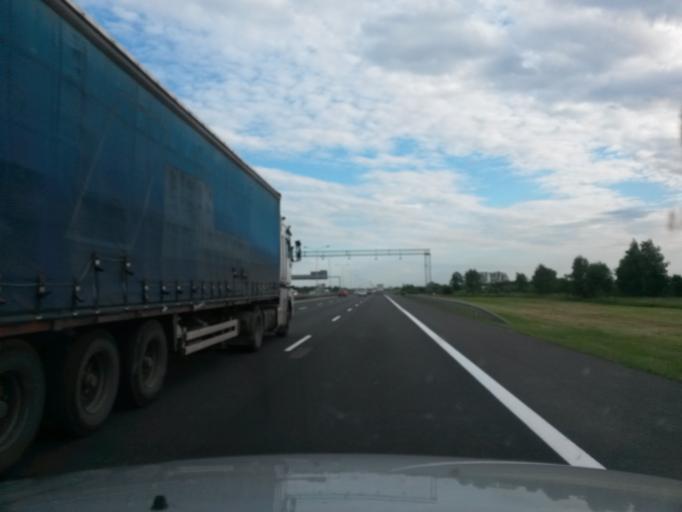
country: PL
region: Lodz Voivodeship
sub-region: Piotrkow Trybunalski
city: Piotrkow Trybunalski
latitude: 51.4221
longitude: 19.6383
